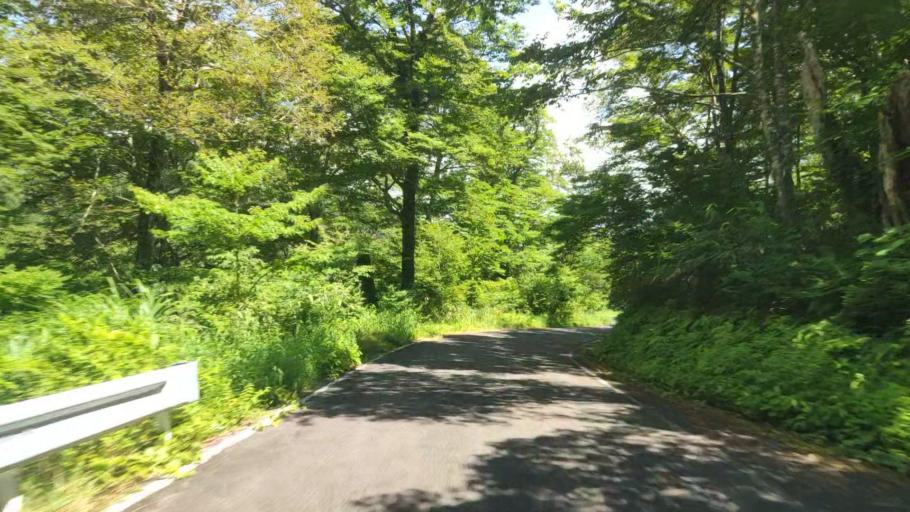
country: JP
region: Fukui
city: Ono
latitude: 35.7751
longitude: 136.5260
